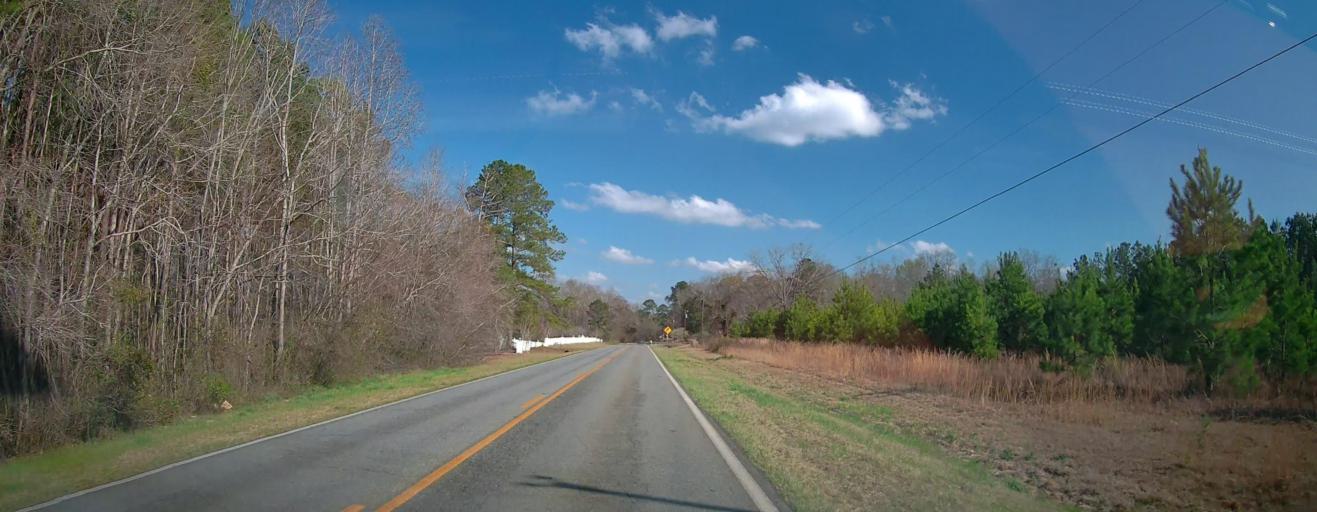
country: US
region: Georgia
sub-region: Laurens County
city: Dublin
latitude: 32.5576
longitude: -83.0015
